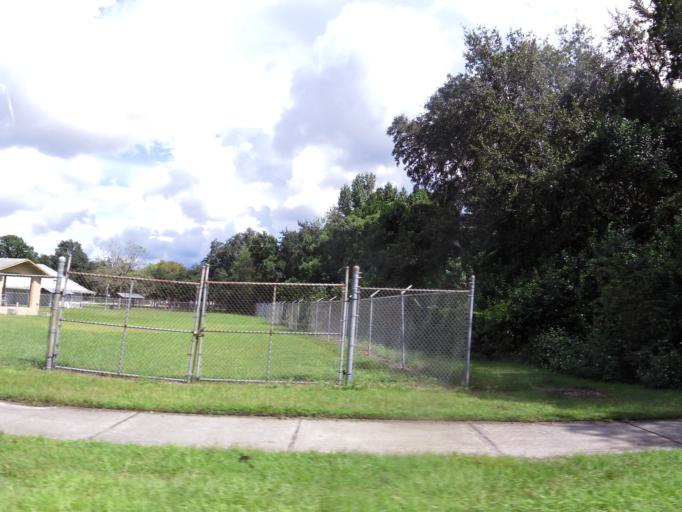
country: US
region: Florida
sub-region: Union County
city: Lake Butler
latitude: 30.0214
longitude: -82.3421
